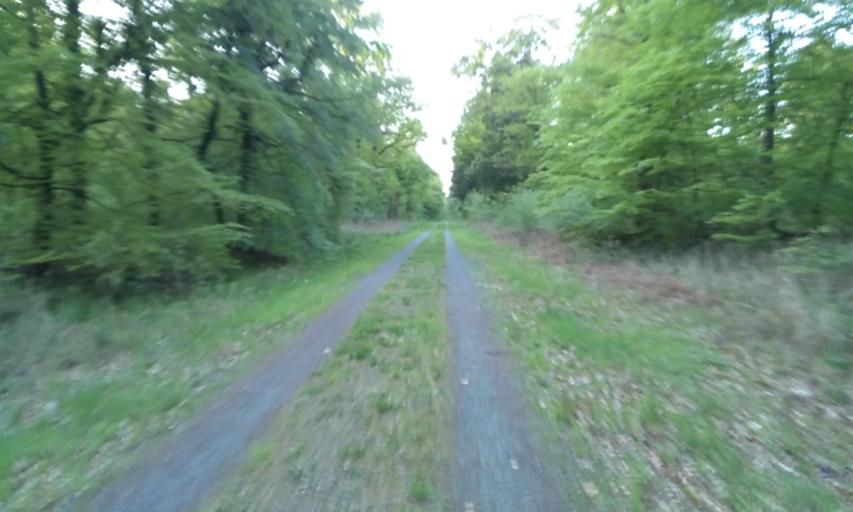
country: DE
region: Lower Saxony
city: Harsefeld
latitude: 53.4159
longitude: 9.5033
